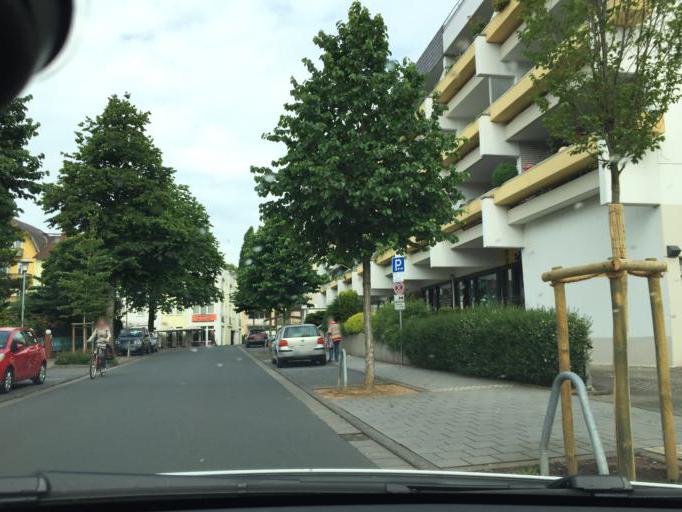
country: DE
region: Lower Saxony
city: Bad Pyrmont
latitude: 51.9844
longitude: 9.2560
